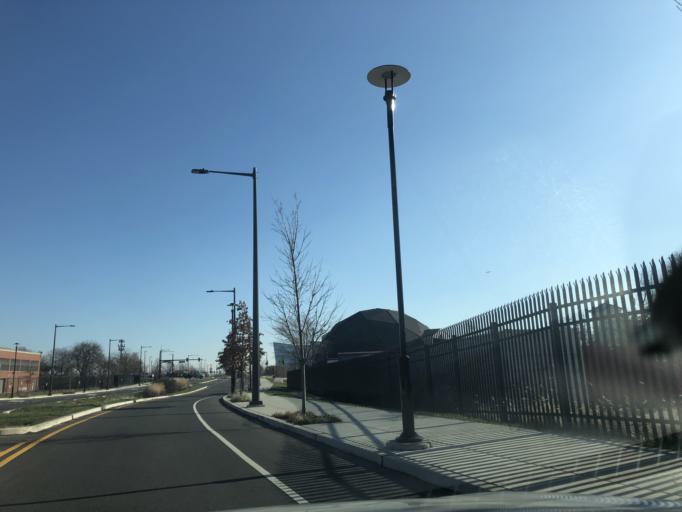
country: US
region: New Jersey
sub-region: Gloucester County
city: National Park
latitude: 39.8976
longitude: -75.1781
